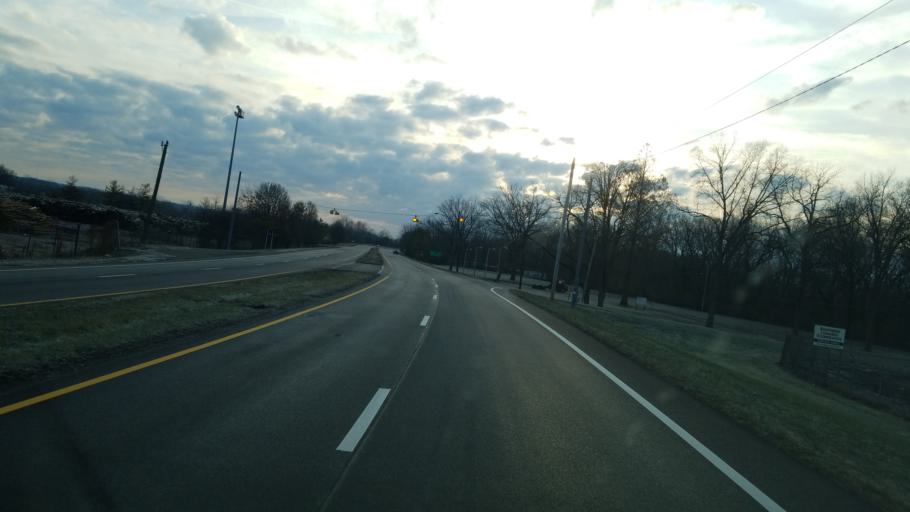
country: US
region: Ohio
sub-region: Ross County
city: Chillicothe
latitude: 39.3208
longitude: -82.9693
